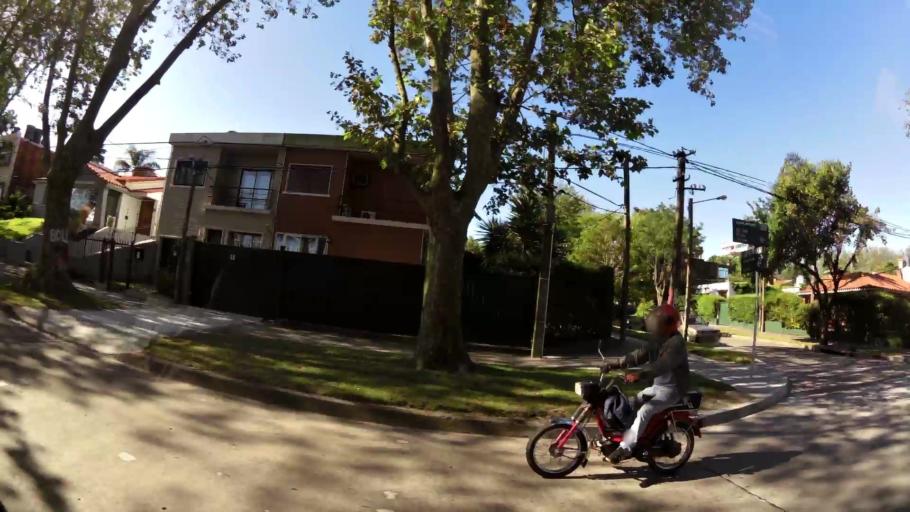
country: UY
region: Canelones
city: Paso de Carrasco
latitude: -34.8907
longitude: -56.0873
